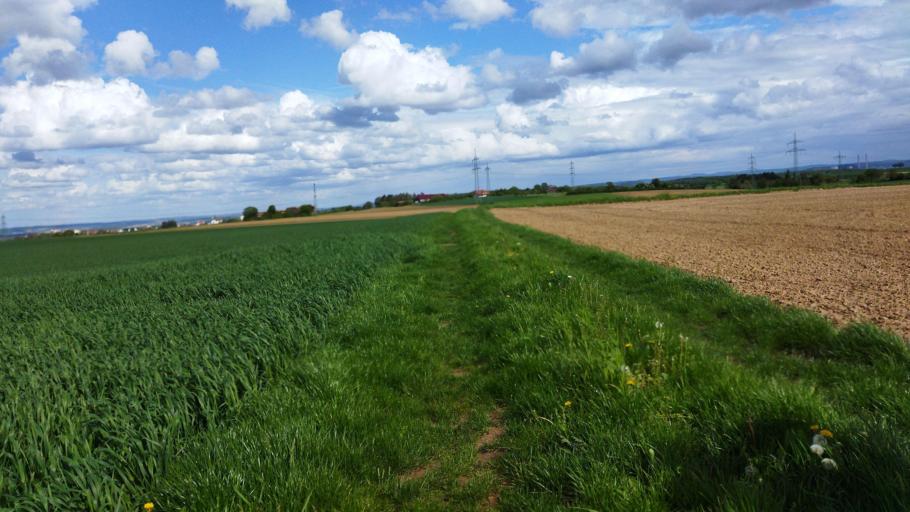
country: DE
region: Baden-Wuerttemberg
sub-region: Regierungsbezirk Stuttgart
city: Bad Rappenau
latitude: 49.2277
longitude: 9.1248
